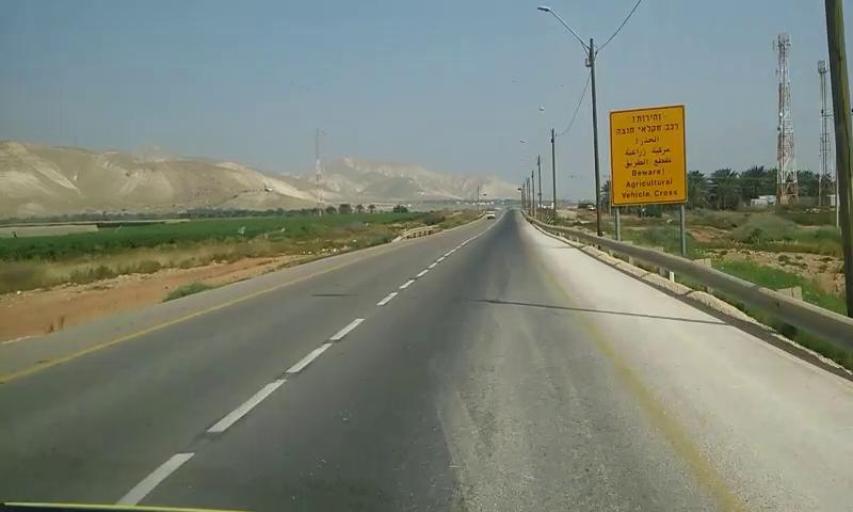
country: PS
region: West Bank
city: Al Fasayil
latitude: 32.0409
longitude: 35.4592
